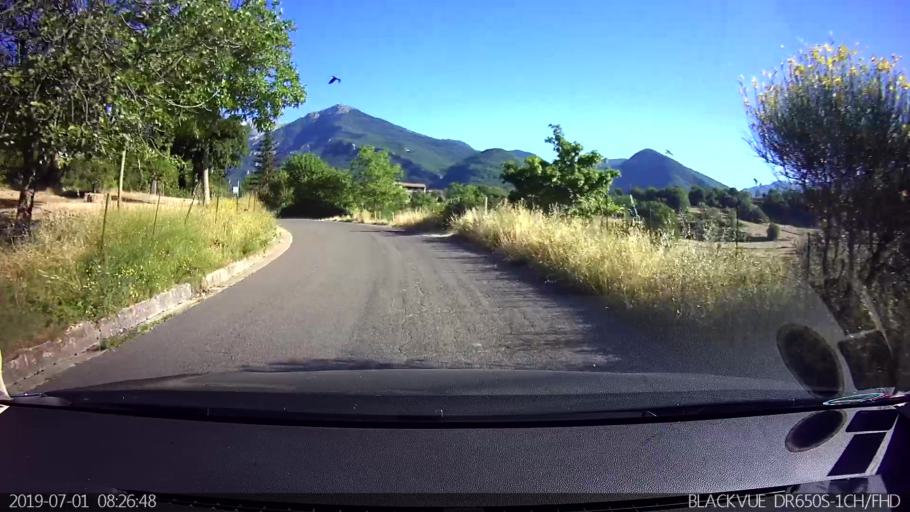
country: IT
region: Latium
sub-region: Provincia di Frosinone
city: Collepardo
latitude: 41.7709
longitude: 13.4049
